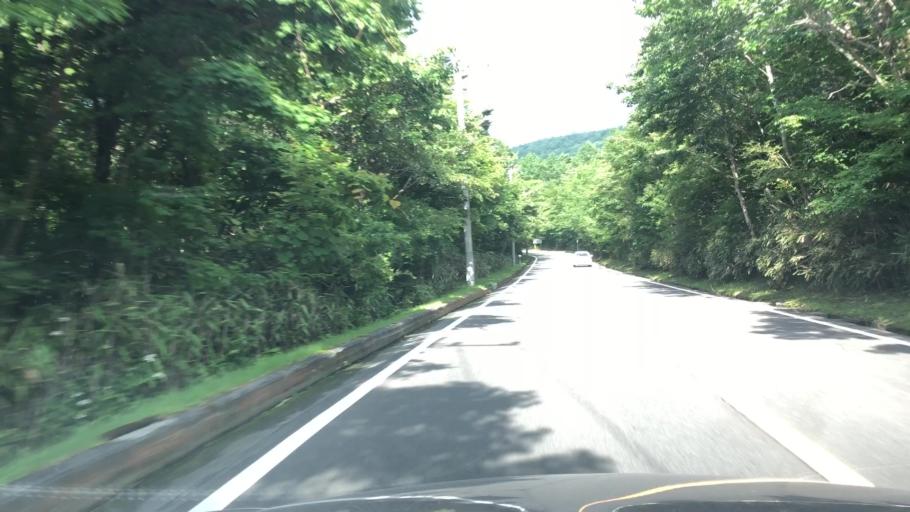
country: JP
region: Shizuoka
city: Gotemba
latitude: 35.3317
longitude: 138.8069
